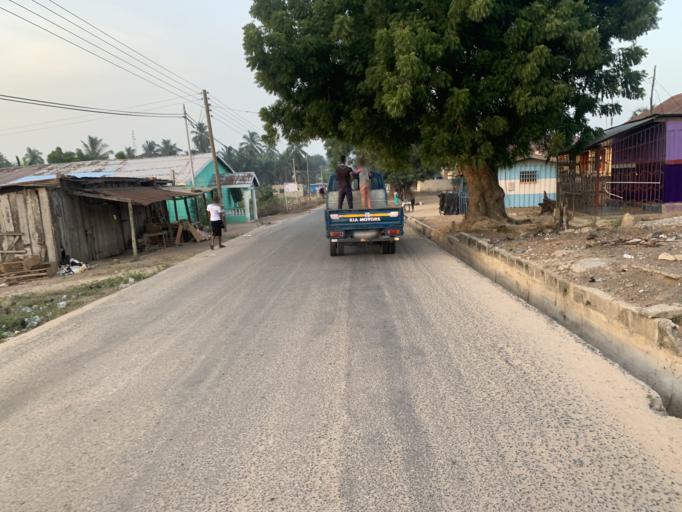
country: GH
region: Central
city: Winneba
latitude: 5.3503
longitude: -0.6279
